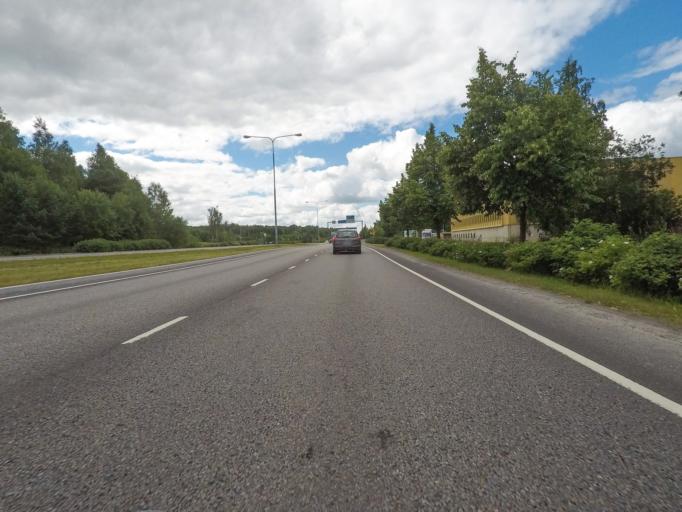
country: FI
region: Varsinais-Suomi
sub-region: Turku
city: Raisio
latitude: 60.4778
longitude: 22.1588
